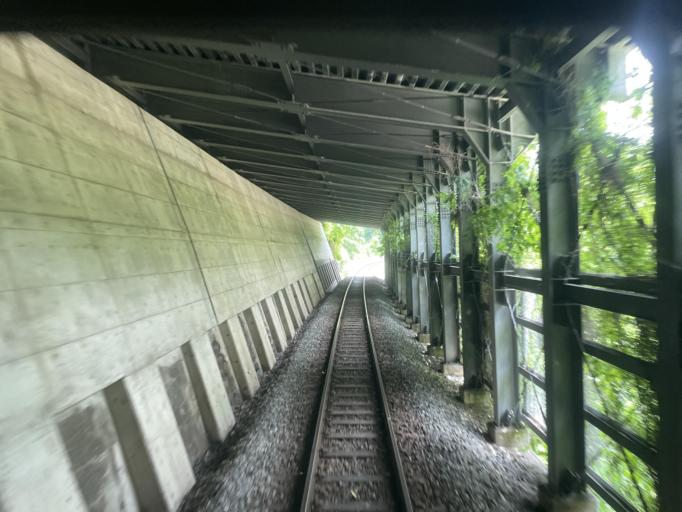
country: JP
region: Nagano
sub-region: Kitaazumi Gun
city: Hakuba
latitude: 36.8588
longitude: 137.8974
